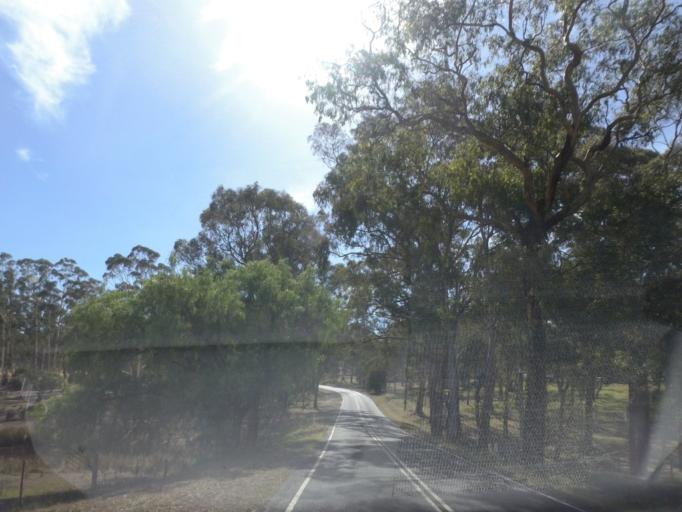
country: AU
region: Victoria
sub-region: Nillumbik
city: Saint Andrews
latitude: -37.6126
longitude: 145.2326
